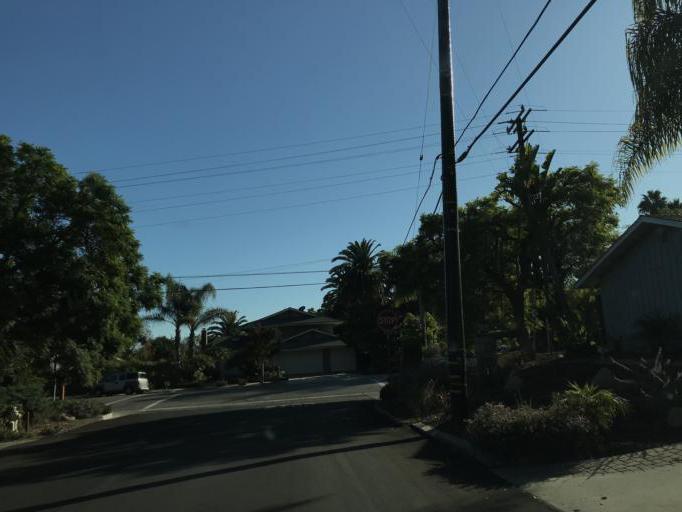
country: US
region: California
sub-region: Santa Barbara County
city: Goleta
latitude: 34.4594
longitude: -119.8162
